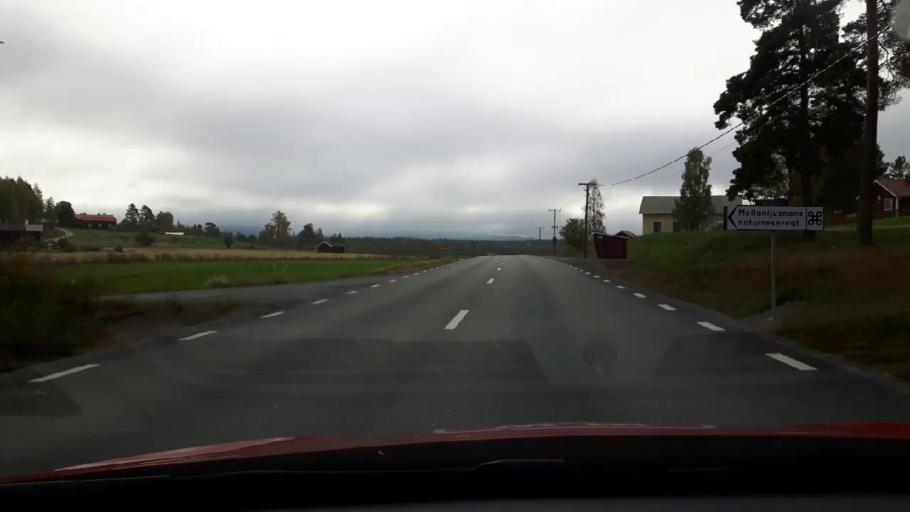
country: SE
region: Gaevleborg
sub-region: Ljusdals Kommun
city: Farila
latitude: 61.8678
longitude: 15.7308
